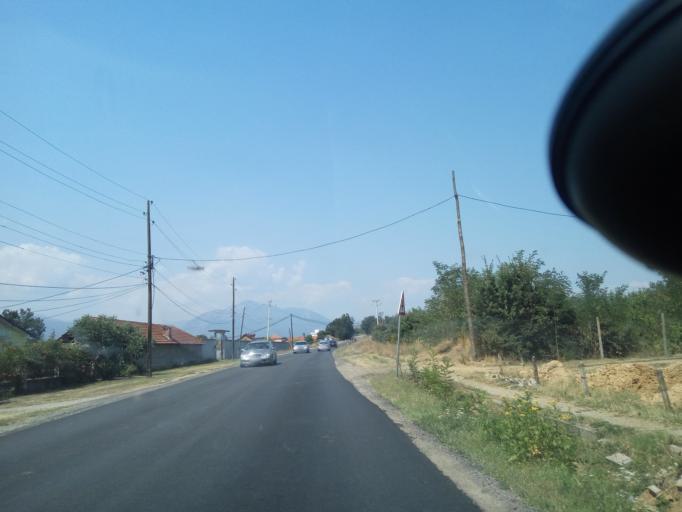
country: XK
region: Gjakova
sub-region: Komuna e Decanit
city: Gllogjan
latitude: 42.4450
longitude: 20.3646
